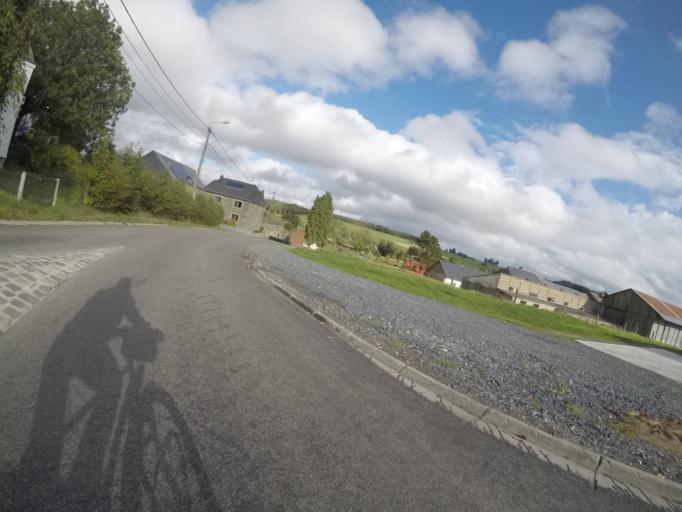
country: BE
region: Wallonia
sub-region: Province du Luxembourg
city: Bastogne
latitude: 49.9531
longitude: 5.6917
